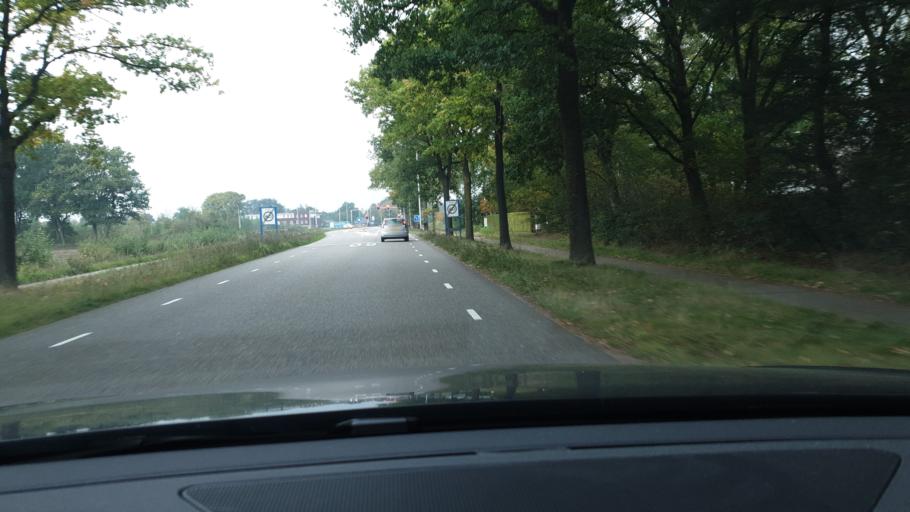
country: NL
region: North Brabant
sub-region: Gemeente Eersel
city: Eersel
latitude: 51.3687
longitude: 5.2791
